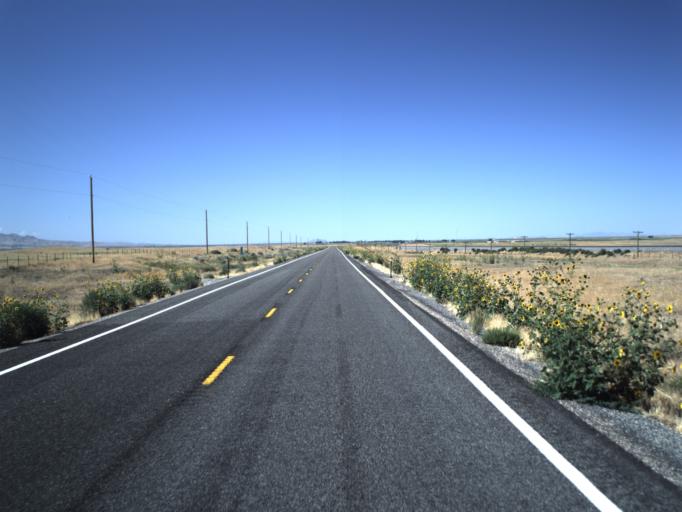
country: US
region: Utah
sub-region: Millard County
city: Delta
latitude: 39.6001
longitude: -112.3253
